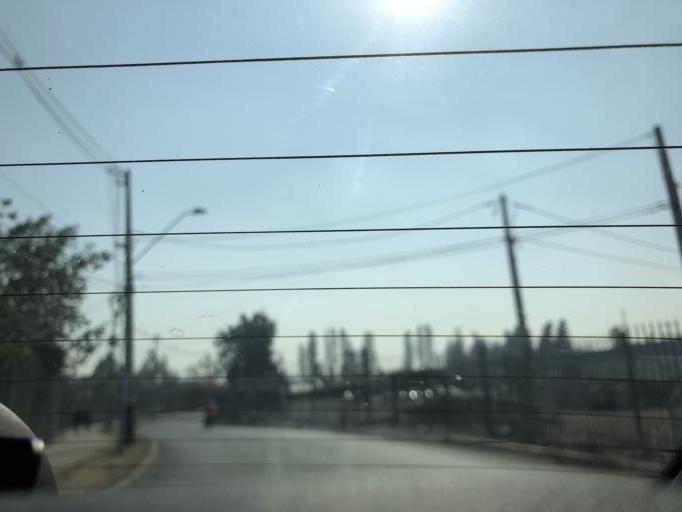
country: CL
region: Santiago Metropolitan
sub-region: Provincia de Cordillera
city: Puente Alto
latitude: -33.6169
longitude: -70.6032
